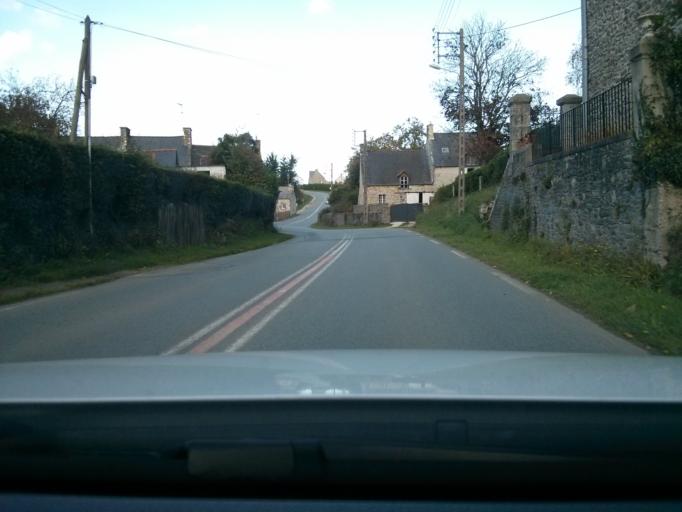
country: FR
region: Brittany
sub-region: Departement des Cotes-d'Armor
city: Pleslin-Trigavou
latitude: 48.5253
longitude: -2.0475
